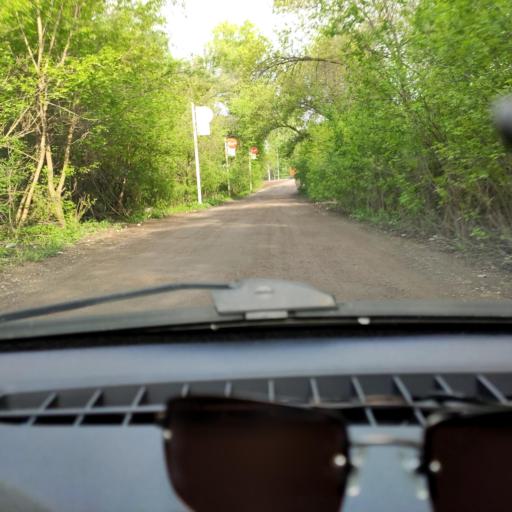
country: RU
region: Bashkortostan
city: Ufa
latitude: 54.6999
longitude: 55.9319
